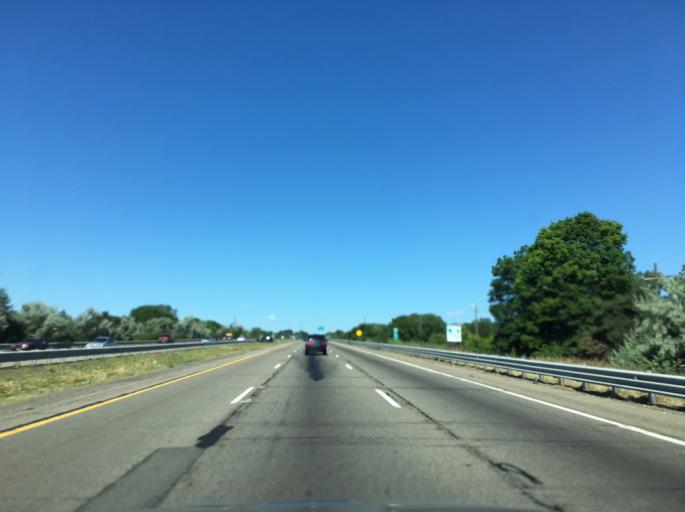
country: US
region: Michigan
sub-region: Oakland County
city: Troy
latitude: 42.6051
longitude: -83.1837
